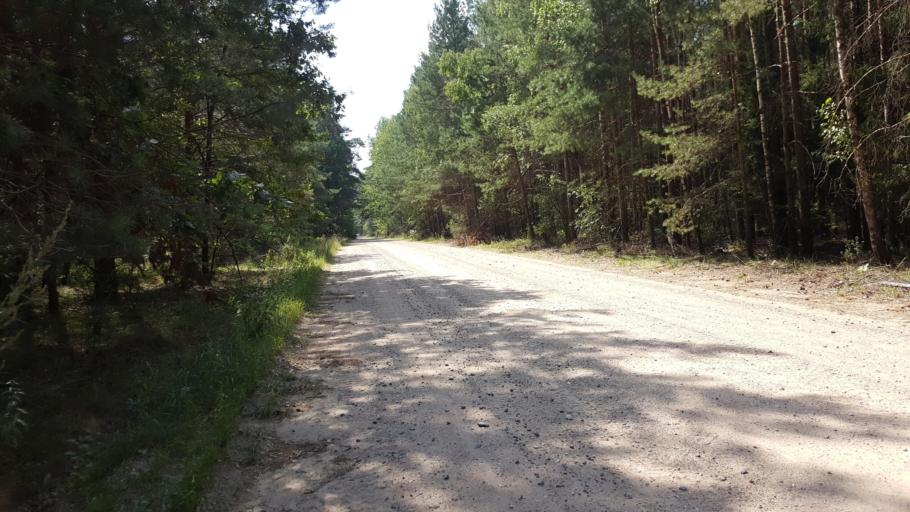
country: PL
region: Podlasie
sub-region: Powiat hajnowski
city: Hajnowka
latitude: 52.5604
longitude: 23.5537
